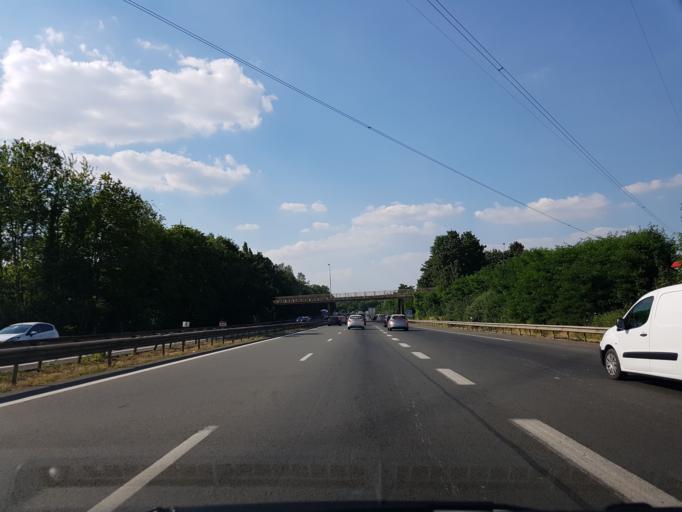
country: FR
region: Nord-Pas-de-Calais
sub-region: Departement du Pas-de-Calais
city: Courcelles-les-Lens
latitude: 50.4145
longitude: 3.0321
